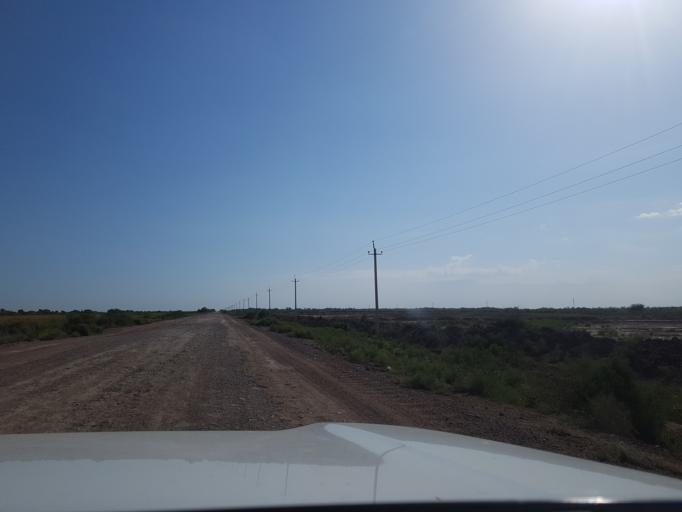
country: TM
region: Dasoguz
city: Koeneuergench
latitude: 42.0328
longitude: 58.8050
